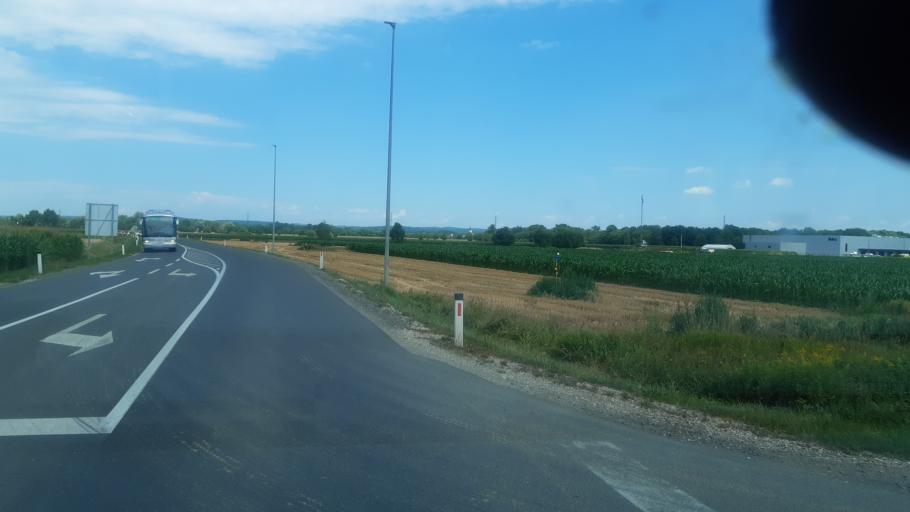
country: SI
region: Murska Sobota
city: Murska Sobota
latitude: 46.6742
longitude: 16.1790
